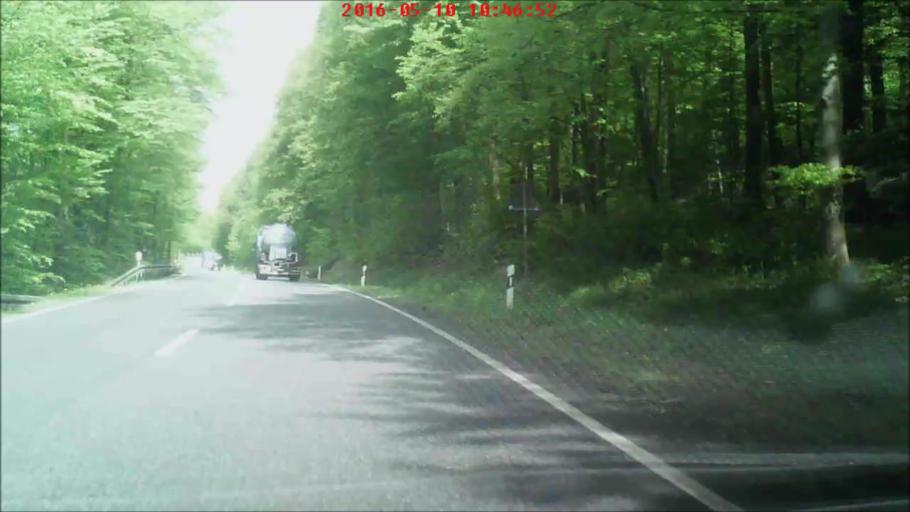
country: DE
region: Hesse
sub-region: Regierungsbezirk Kassel
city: Burghaun
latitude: 50.7456
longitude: 9.6871
